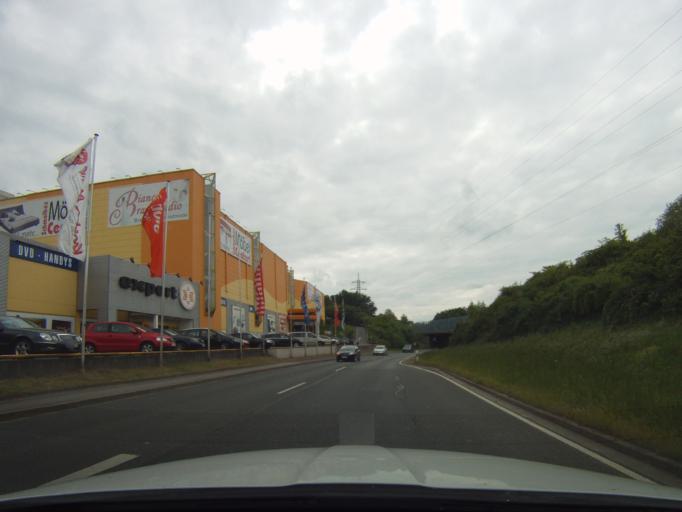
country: DE
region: Bavaria
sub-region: Upper Franconia
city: Lichtenfels
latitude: 50.1392
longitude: 11.0687
